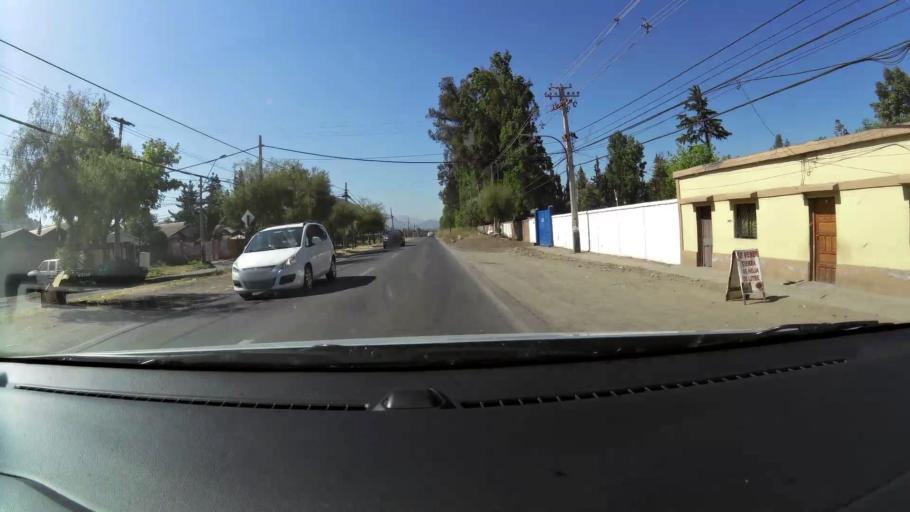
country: CL
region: Santiago Metropolitan
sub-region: Provincia de Maipo
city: San Bernardo
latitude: -33.6117
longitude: -70.6834
